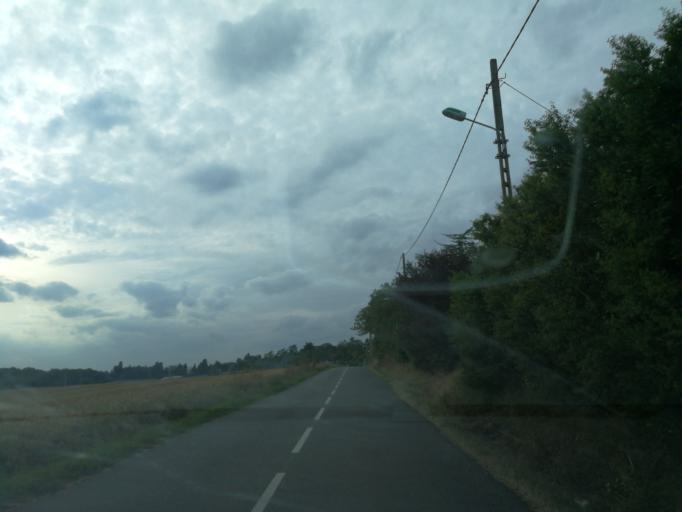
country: FR
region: Midi-Pyrenees
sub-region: Departement de la Haute-Garonne
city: Flourens
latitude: 43.6101
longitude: 1.5357
